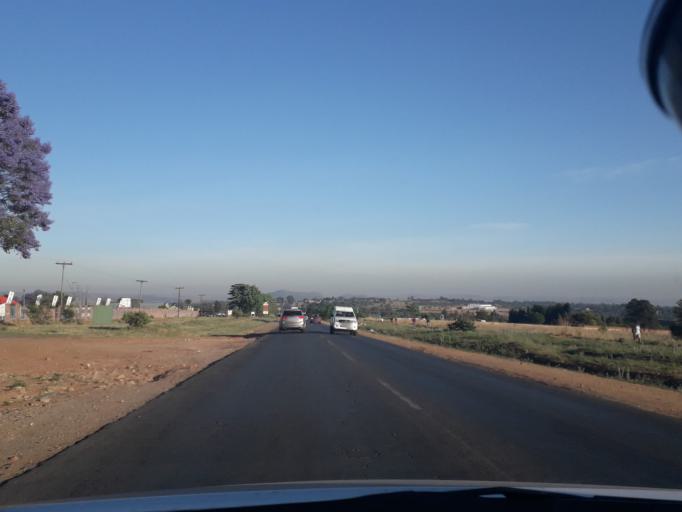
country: ZA
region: Gauteng
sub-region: West Rand District Municipality
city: Muldersdriseloop
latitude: -26.0553
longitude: 27.8965
